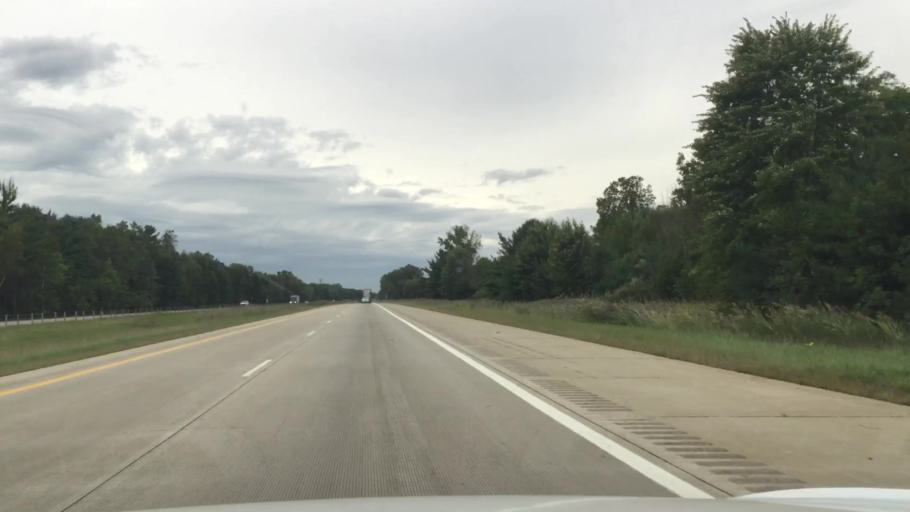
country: US
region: Michigan
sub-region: Saint Clair County
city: Saint Clair
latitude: 42.8333
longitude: -82.5986
